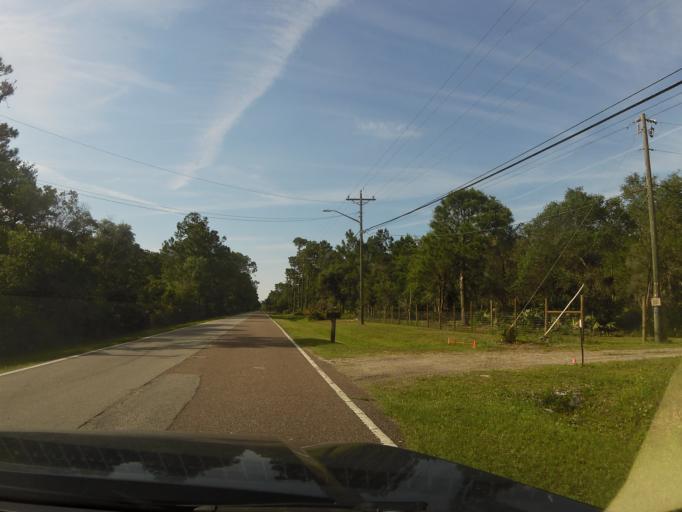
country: US
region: Florida
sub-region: Duval County
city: Atlantic Beach
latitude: 30.4808
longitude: -81.4709
